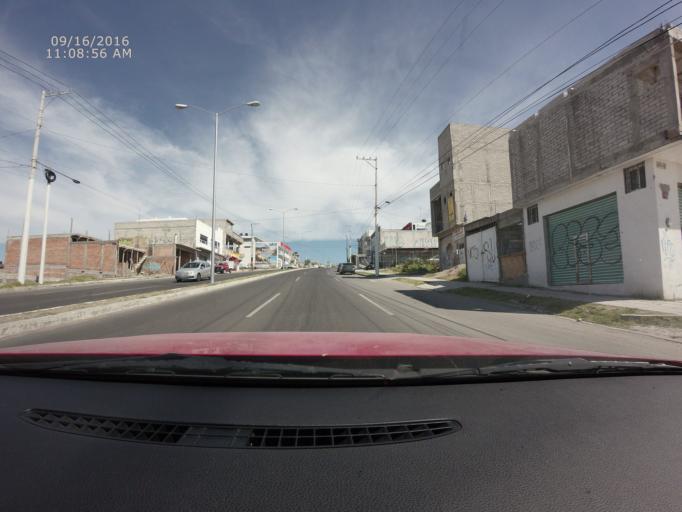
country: MX
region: Queretaro
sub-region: Queretaro
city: Sergio Villasenor
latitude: 20.6357
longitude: -100.4144
